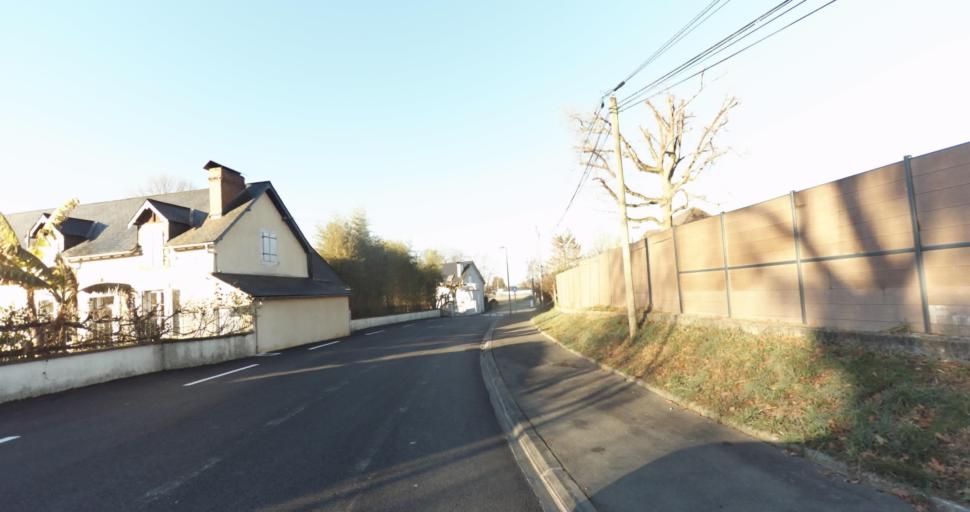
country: FR
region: Aquitaine
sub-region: Departement des Pyrenees-Atlantiques
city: Buros
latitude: 43.3278
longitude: -0.2835
